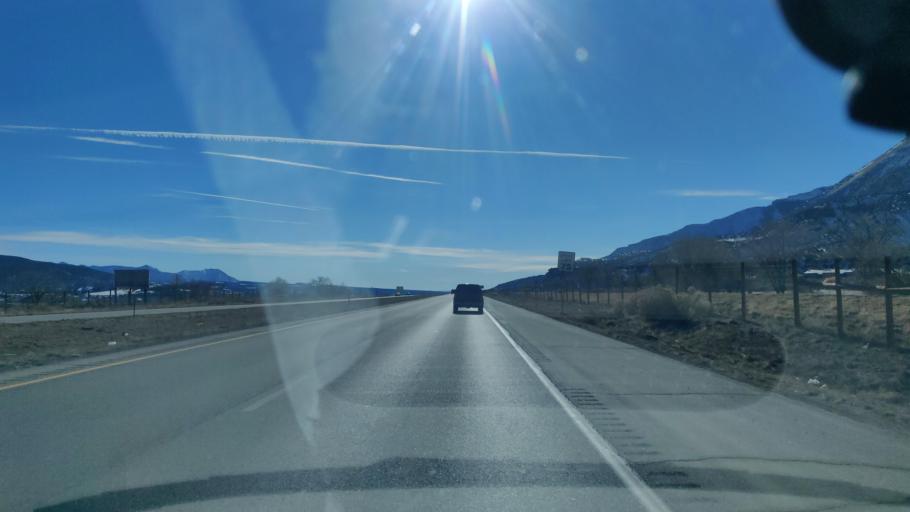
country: US
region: Colorado
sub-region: Garfield County
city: Parachute
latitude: 39.4494
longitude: -108.0550
